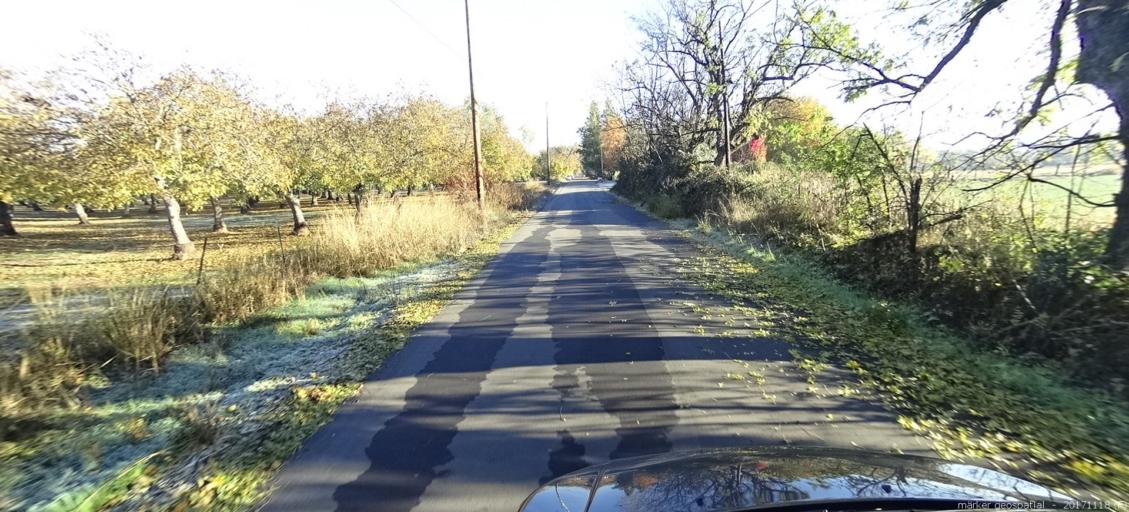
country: US
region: California
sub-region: Shasta County
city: Anderson
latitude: 40.4540
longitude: -122.2573
